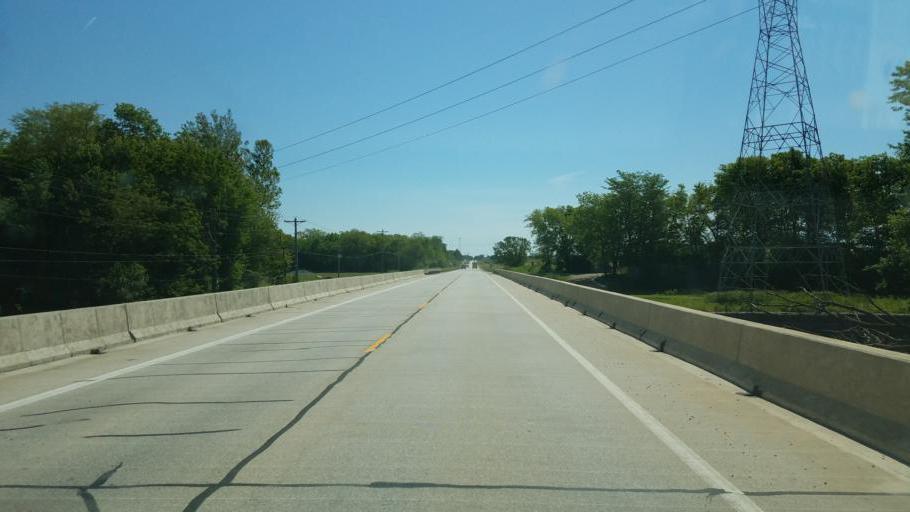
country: US
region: Illinois
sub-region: McLean County
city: Heyworth
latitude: 40.3121
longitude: -89.0152
